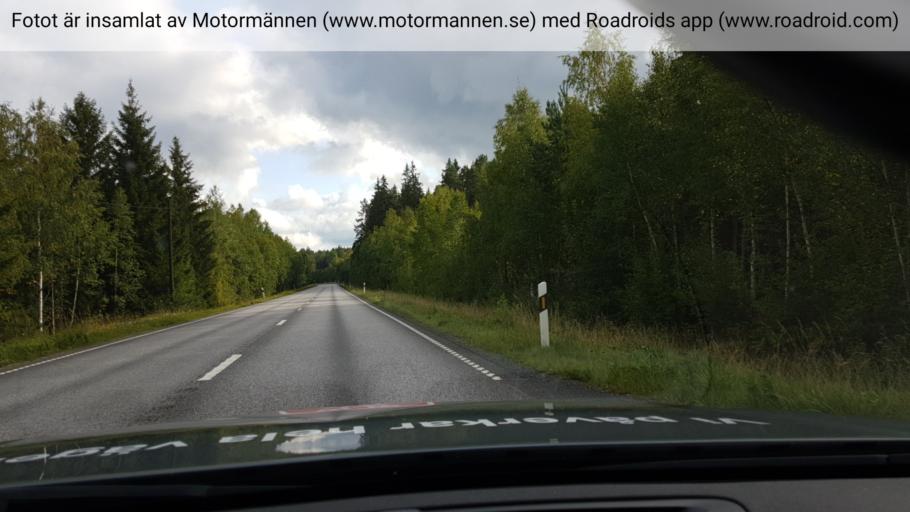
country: SE
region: Stockholm
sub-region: Norrtalje Kommun
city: Hallstavik
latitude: 59.9791
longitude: 18.5975
